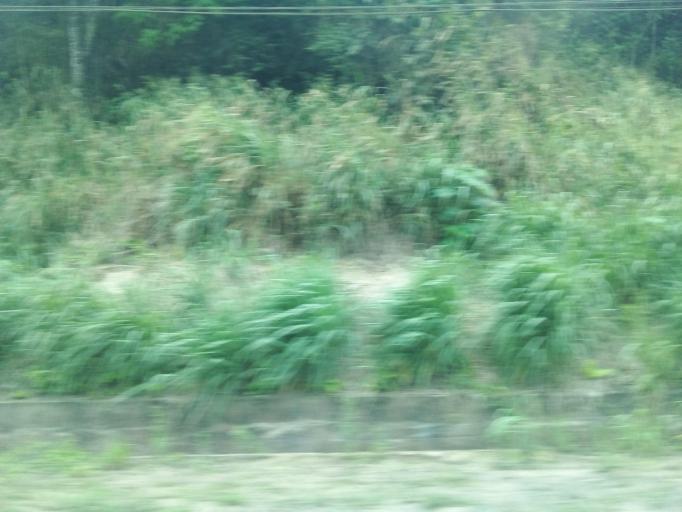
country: BR
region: Minas Gerais
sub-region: Nova Era
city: Nova Era
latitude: -19.7316
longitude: -42.9995
